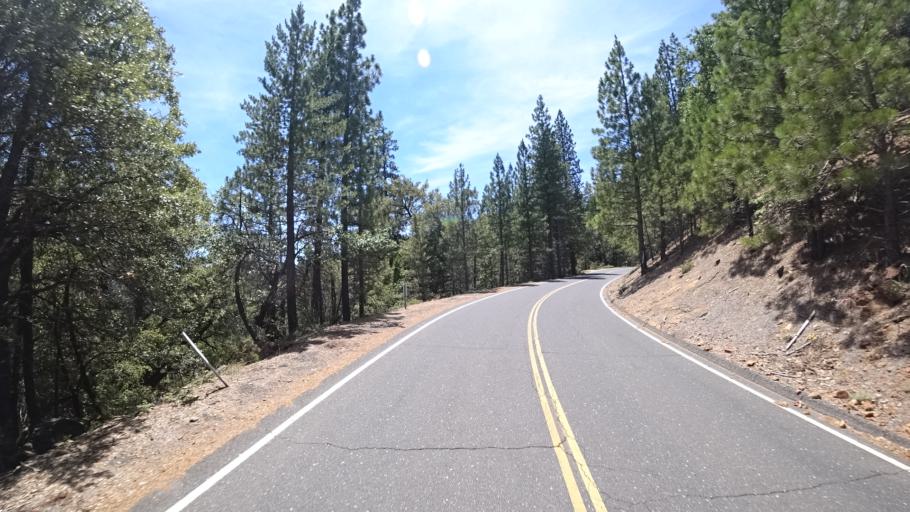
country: US
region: California
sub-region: Calaveras County
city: Arnold
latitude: 38.3082
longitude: -120.2416
